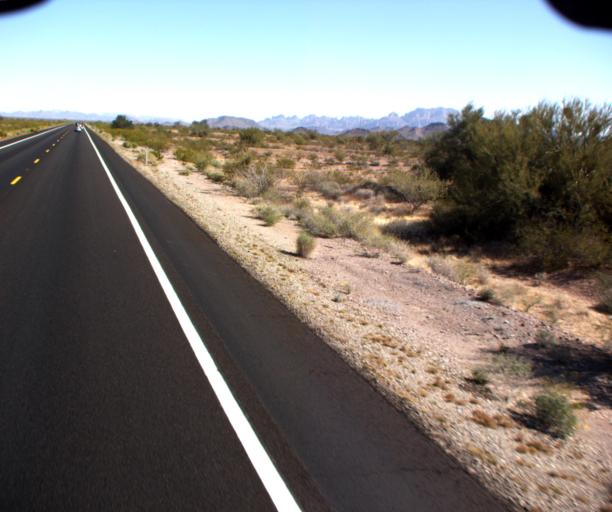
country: US
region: Arizona
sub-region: La Paz County
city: Quartzsite
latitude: 33.2822
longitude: -114.2304
